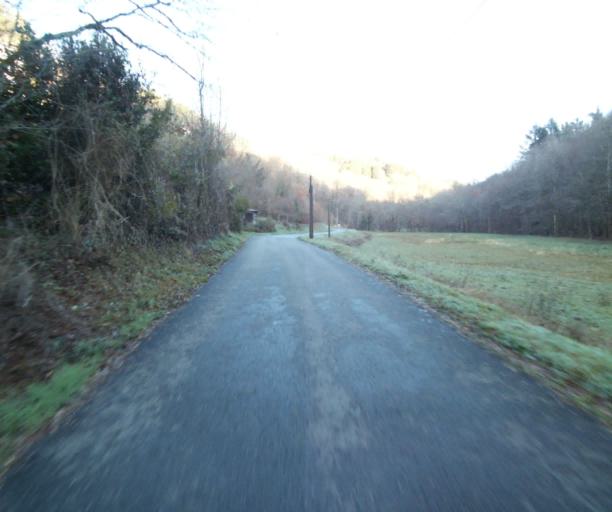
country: FR
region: Limousin
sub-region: Departement de la Correze
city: Laguenne
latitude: 45.2400
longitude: 1.7915
